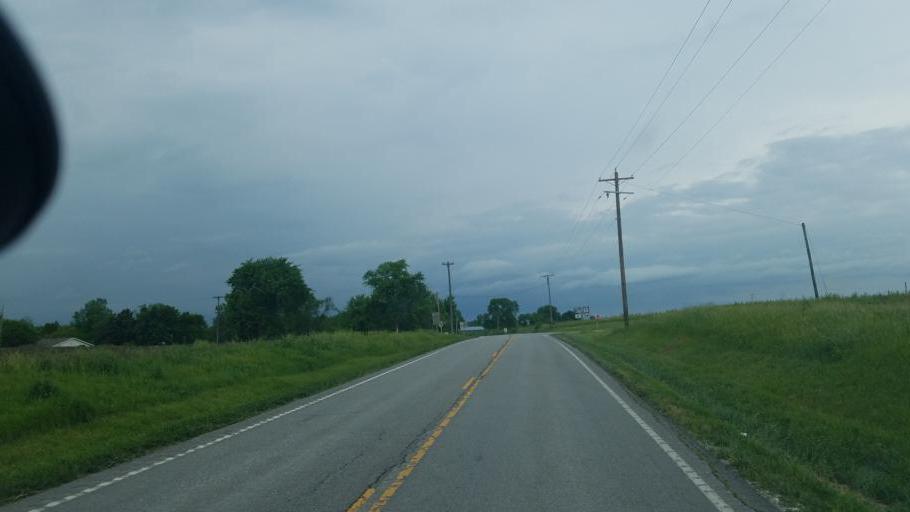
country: US
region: Missouri
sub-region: Cooper County
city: Boonville
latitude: 38.8858
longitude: -92.6521
